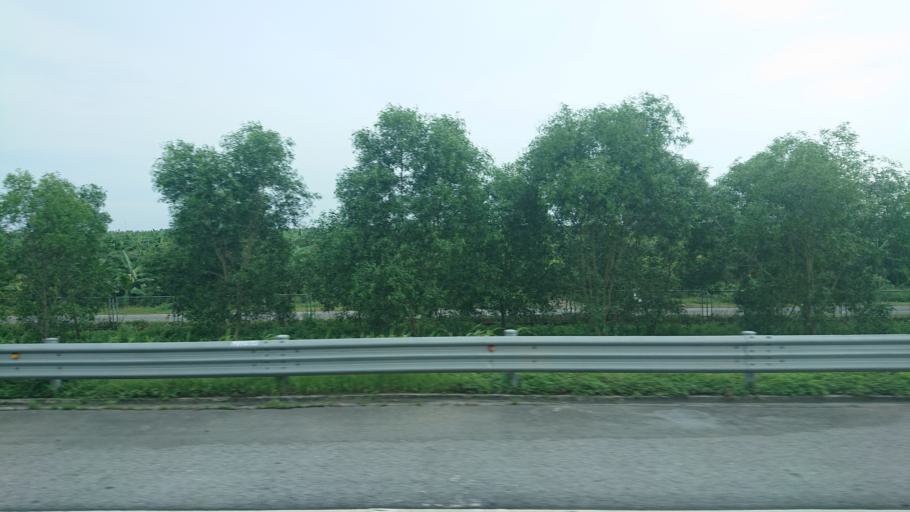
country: VN
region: Hai Duong
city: Tu Ky
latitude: 20.8263
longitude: 106.4608
